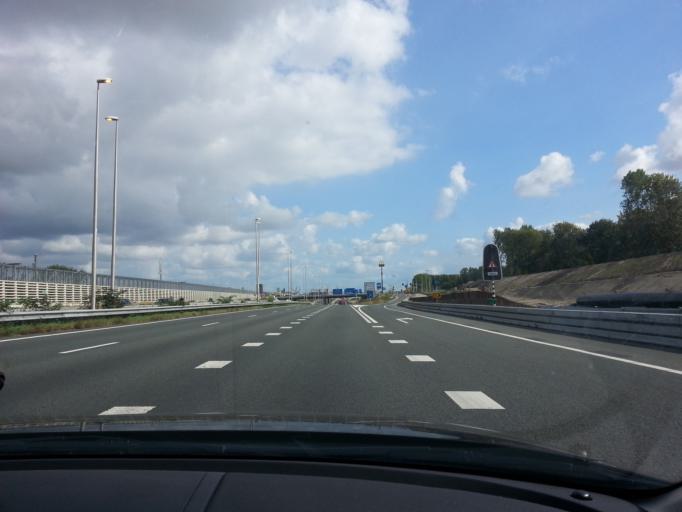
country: NL
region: South Holland
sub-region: Gemeente Spijkenisse
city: Spijkenisse
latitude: 51.8752
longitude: 4.3520
